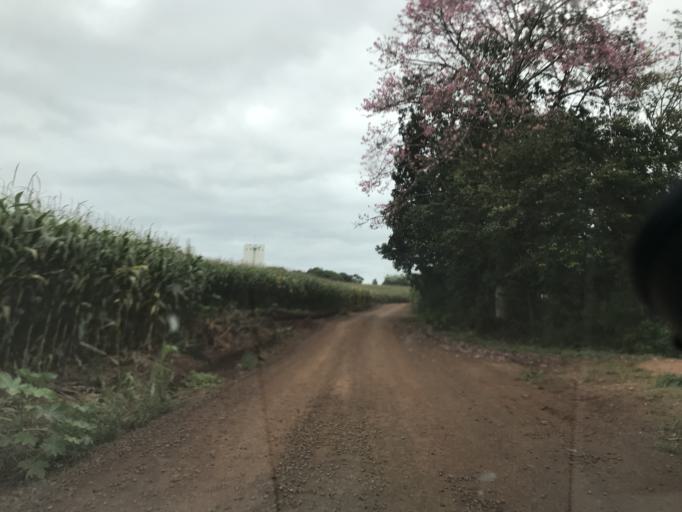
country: BR
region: Parana
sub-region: Palotina
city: Palotina
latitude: -24.3042
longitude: -53.8293
